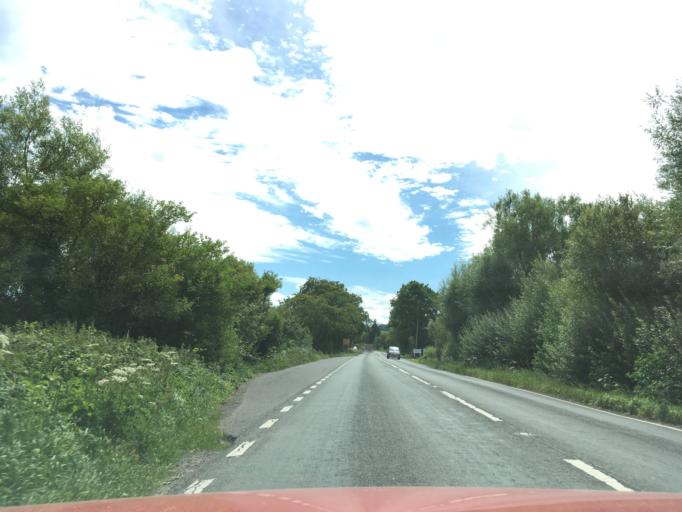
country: GB
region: England
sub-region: Somerset
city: Glastonbury
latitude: 51.1705
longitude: -2.6964
